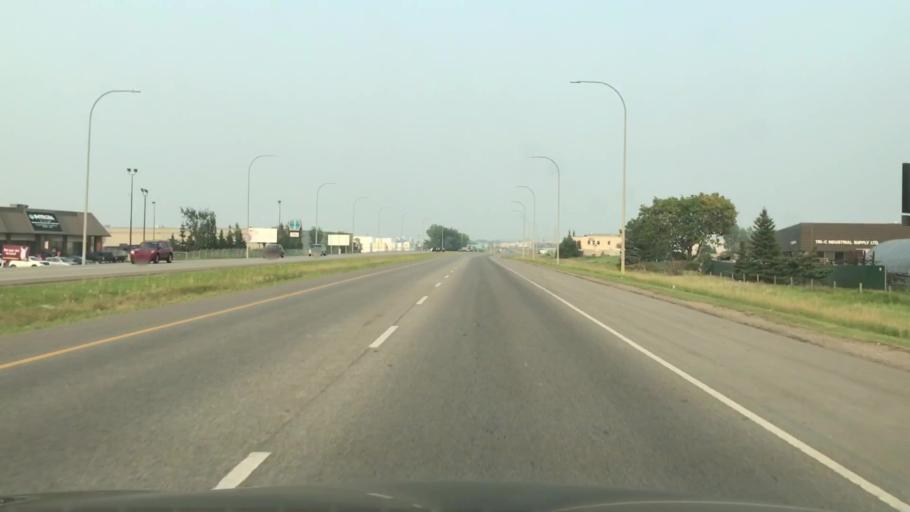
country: CA
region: Alberta
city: Edmonton
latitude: 53.5159
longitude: -113.4078
